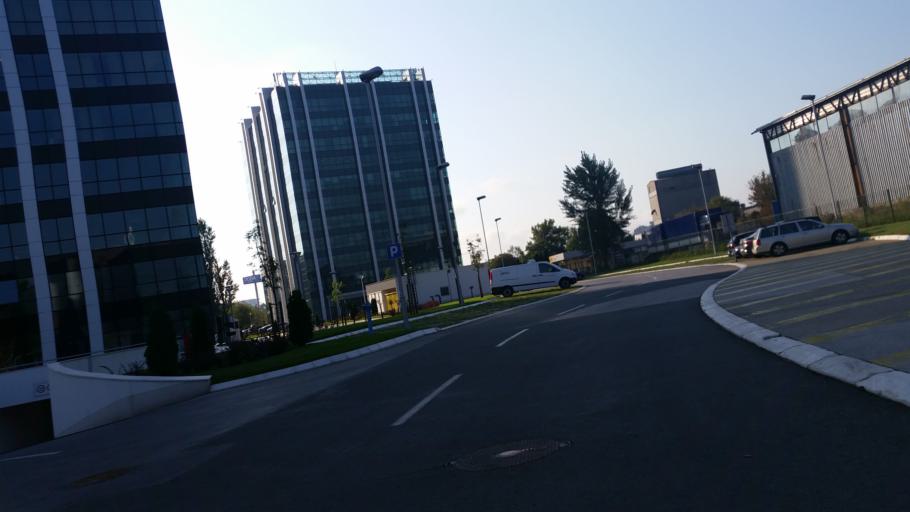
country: RS
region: Central Serbia
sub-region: Belgrade
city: Novi Beograd
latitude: 44.8131
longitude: 20.3946
